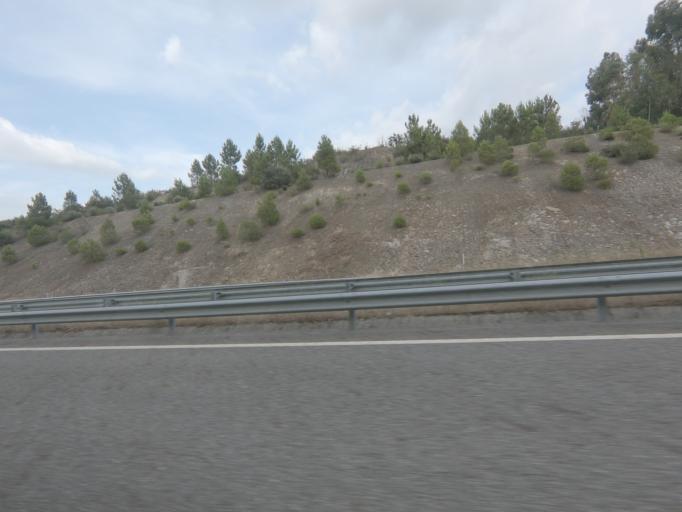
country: PT
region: Vila Real
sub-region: Chaves
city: Chaves
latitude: 41.6975
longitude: -7.5526
